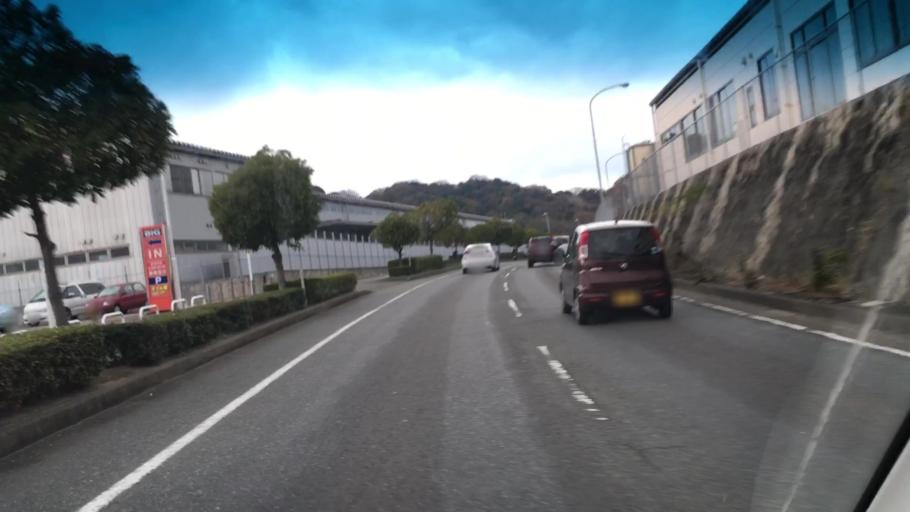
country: JP
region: Fukuoka
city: Maebaru-chuo
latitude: 33.5687
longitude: 130.2949
